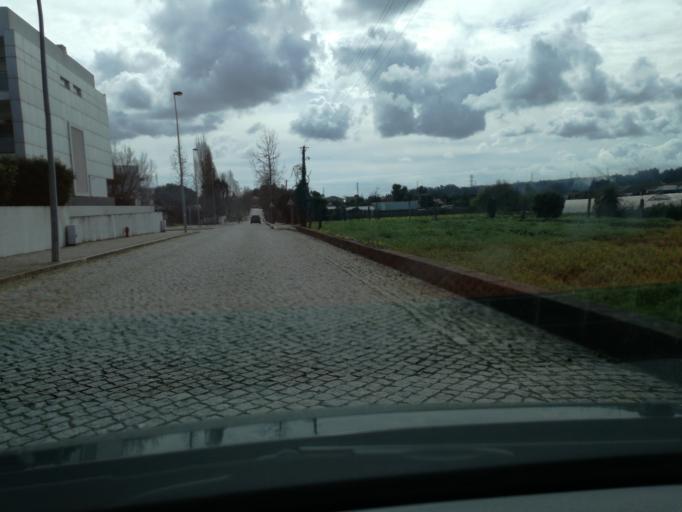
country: PT
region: Porto
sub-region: Valongo
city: Ermesinde
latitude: 41.2484
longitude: -8.5492
